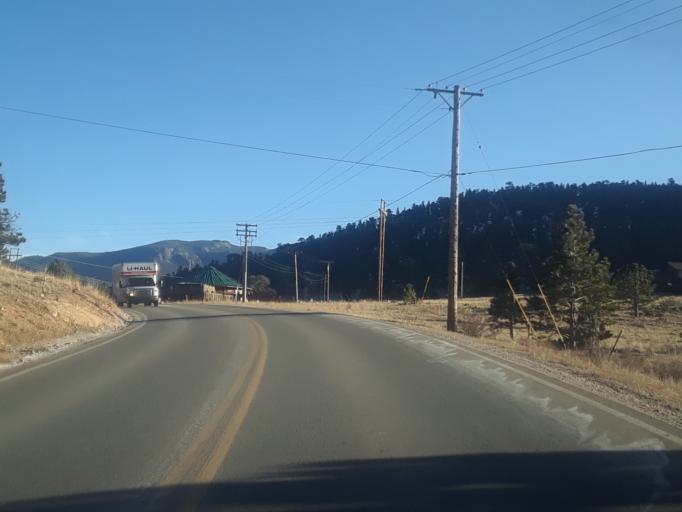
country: US
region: Colorado
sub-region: Larimer County
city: Estes Park
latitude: 40.3483
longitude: -105.5387
